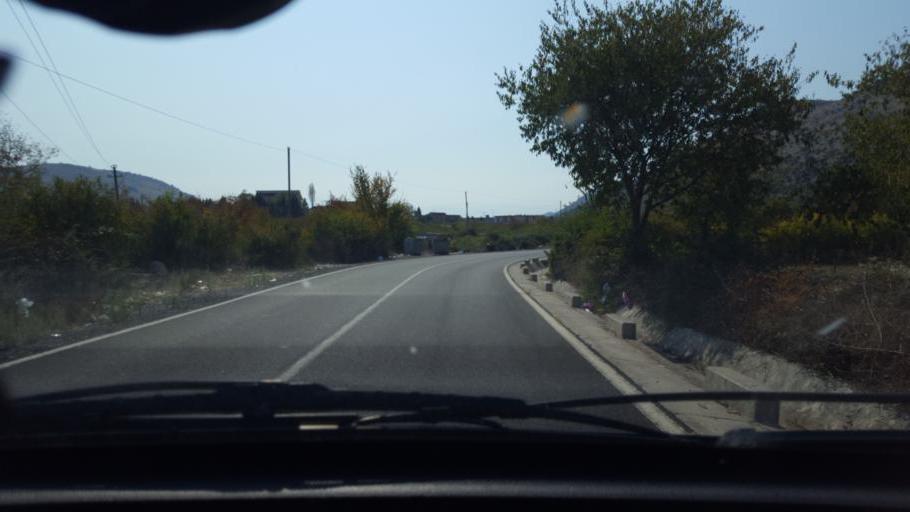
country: AL
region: Shkoder
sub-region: Rrethi i Malesia e Madhe
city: Hot
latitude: 42.3394
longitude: 19.4363
